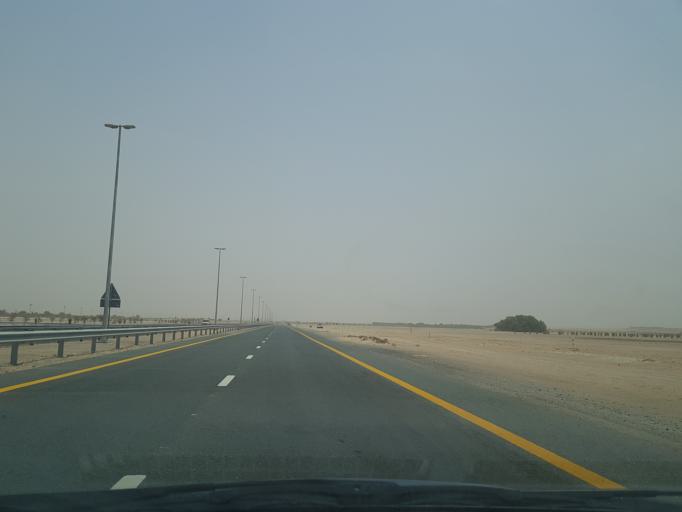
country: AE
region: Dubai
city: Dubai
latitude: 24.8716
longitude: 55.4154
